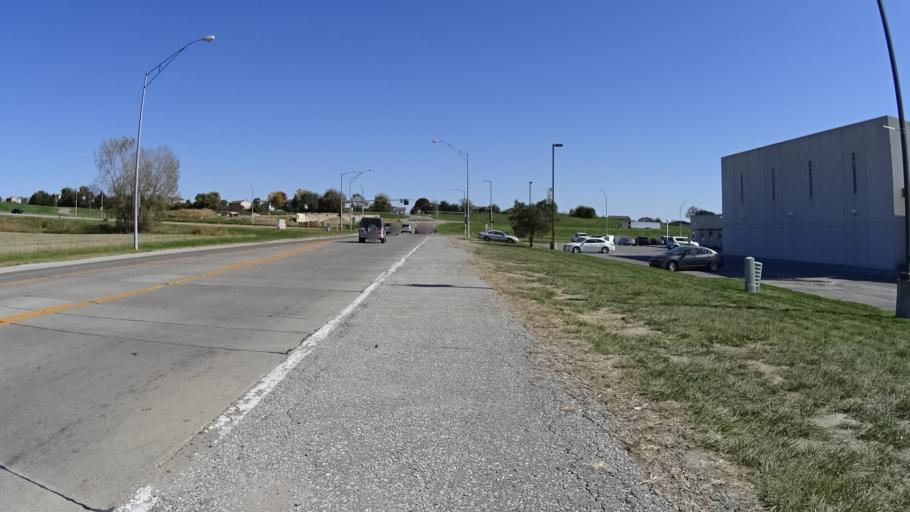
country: US
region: Nebraska
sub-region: Sarpy County
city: Papillion
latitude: 41.1565
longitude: -96.0246
